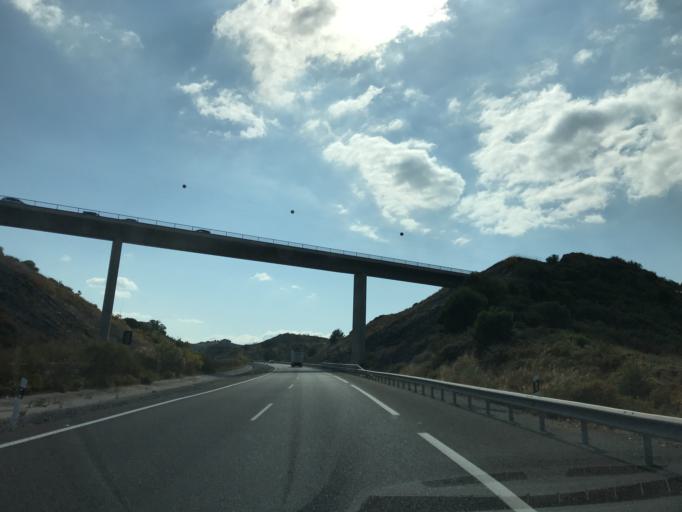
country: ES
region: Andalusia
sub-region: Provincia de Malaga
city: Istan
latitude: 36.5265
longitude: -4.9681
